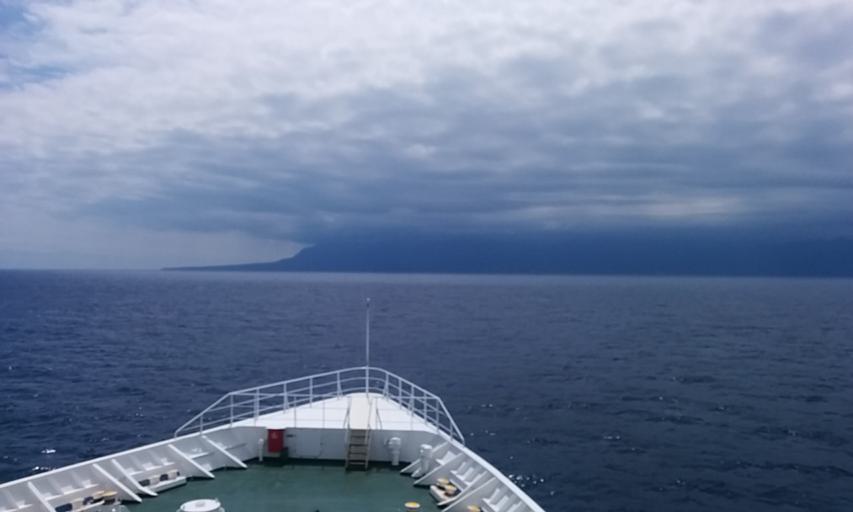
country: JP
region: Kagoshima
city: Nishinoomote
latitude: 30.5434
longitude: 130.6166
